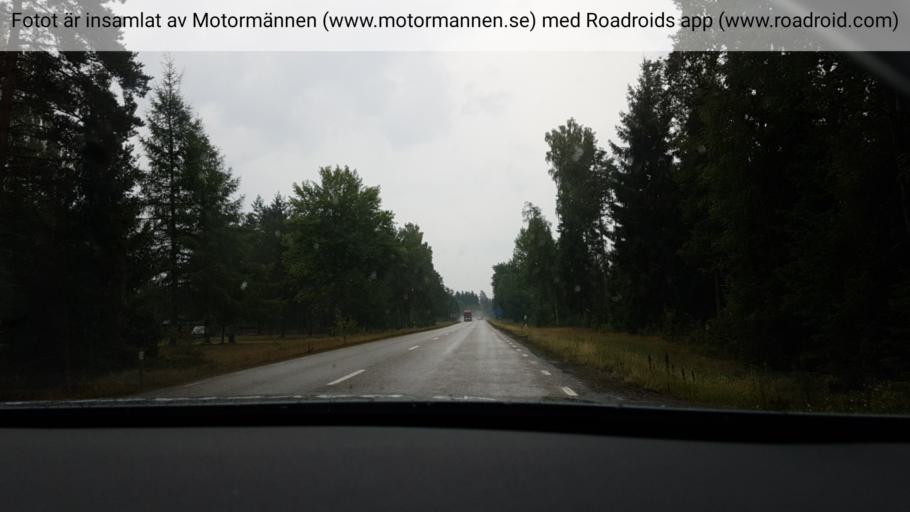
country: SE
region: Joenkoeping
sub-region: Jonkopings Kommun
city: Odensjo
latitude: 57.6100
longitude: 14.2122
